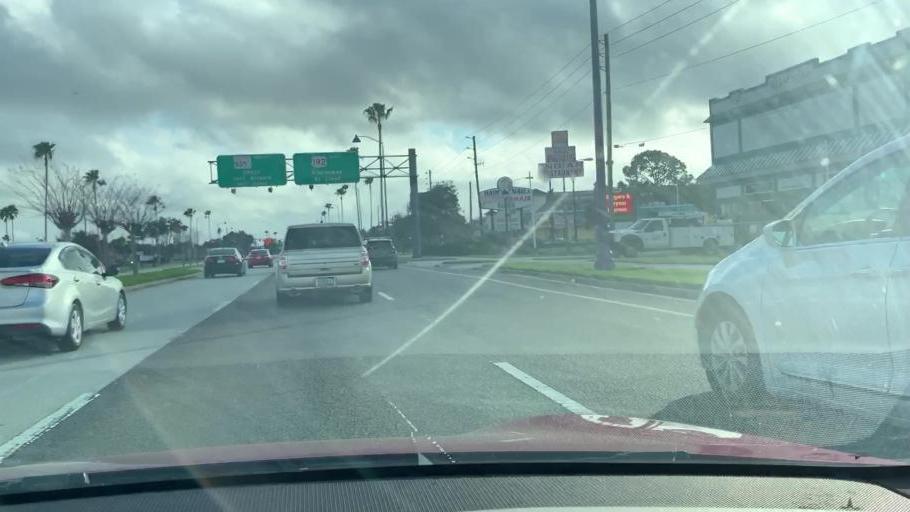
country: US
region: Florida
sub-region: Osceola County
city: Celebration
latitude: 28.3329
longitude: -81.4832
